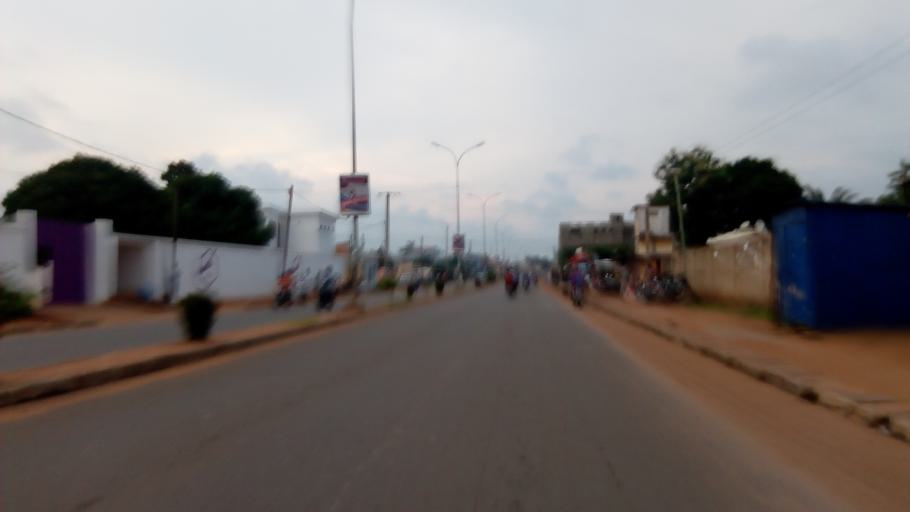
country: TG
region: Maritime
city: Lome
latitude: 6.2128
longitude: 1.2008
